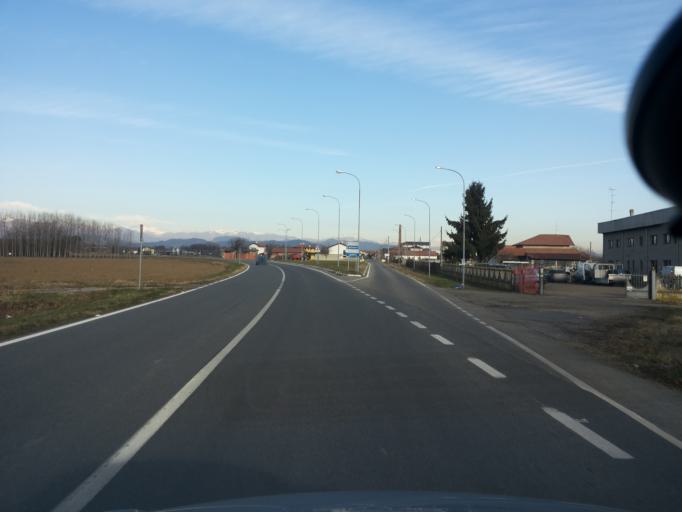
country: IT
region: Piedmont
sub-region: Provincia di Vercelli
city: Lenta
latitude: 45.5479
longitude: 8.3848
